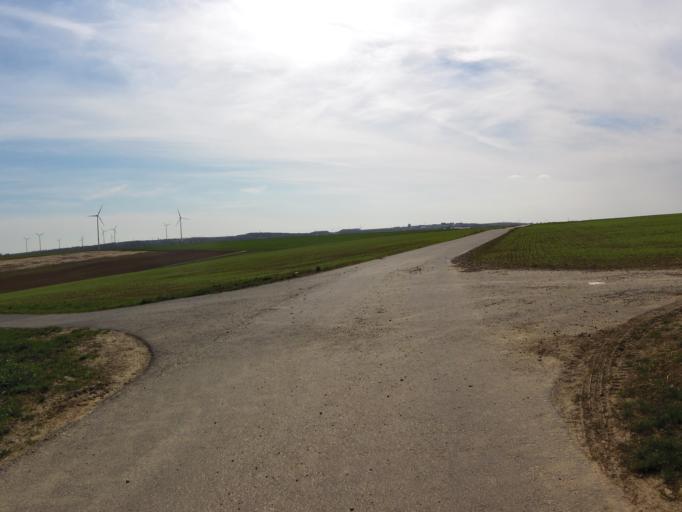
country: DE
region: Bavaria
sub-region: Regierungsbezirk Unterfranken
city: Mainstockheim
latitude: 49.7953
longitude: 10.1364
